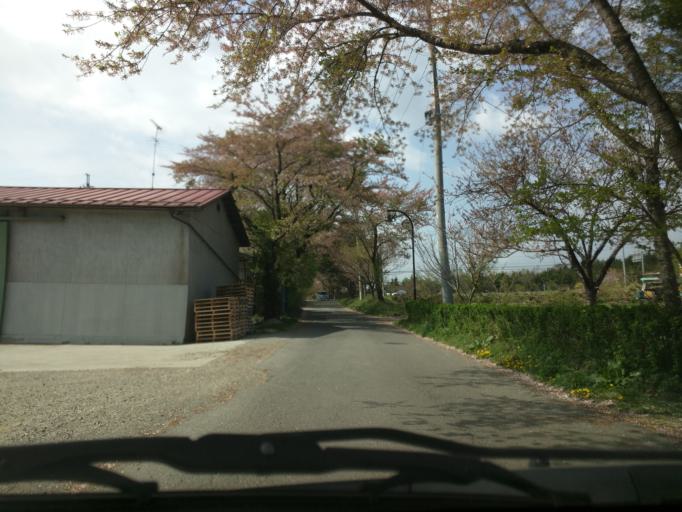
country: JP
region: Fukushima
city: Nihommatsu
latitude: 37.6031
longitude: 140.3595
